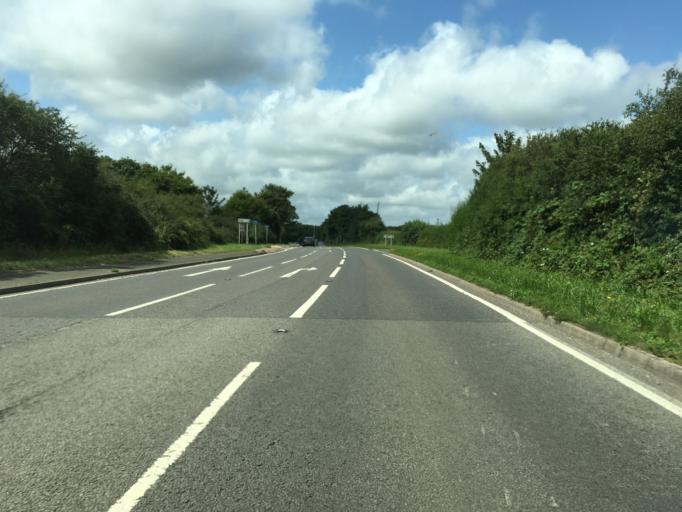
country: GB
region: England
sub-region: East Sussex
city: Pevensey
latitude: 50.8488
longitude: 0.3904
